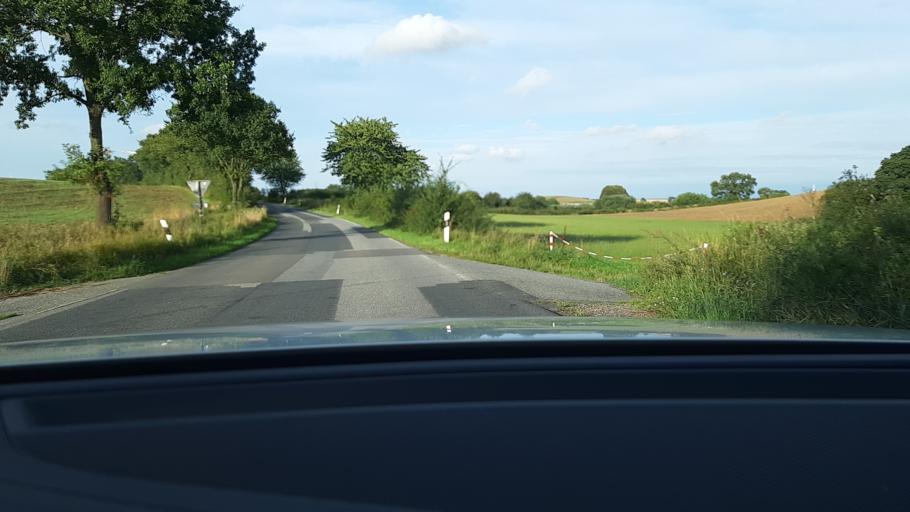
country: DE
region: Schleswig-Holstein
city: Monkhagen
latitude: 53.9053
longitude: 10.5496
